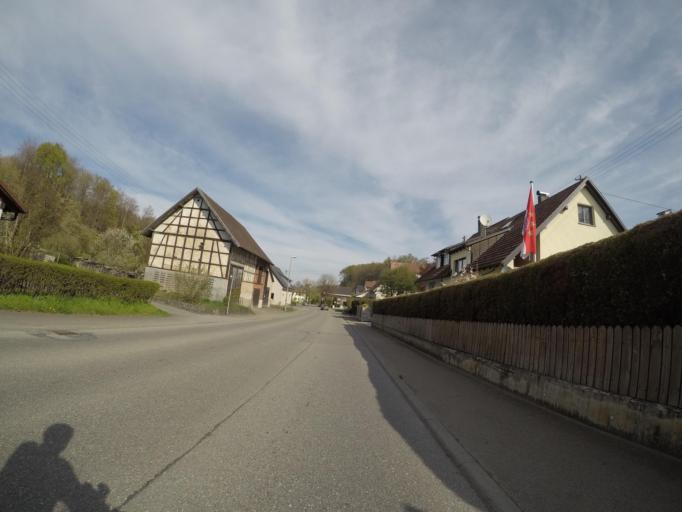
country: DE
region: Baden-Wuerttemberg
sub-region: Tuebingen Region
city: Allmannsweiler
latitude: 48.0065
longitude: 9.5638
